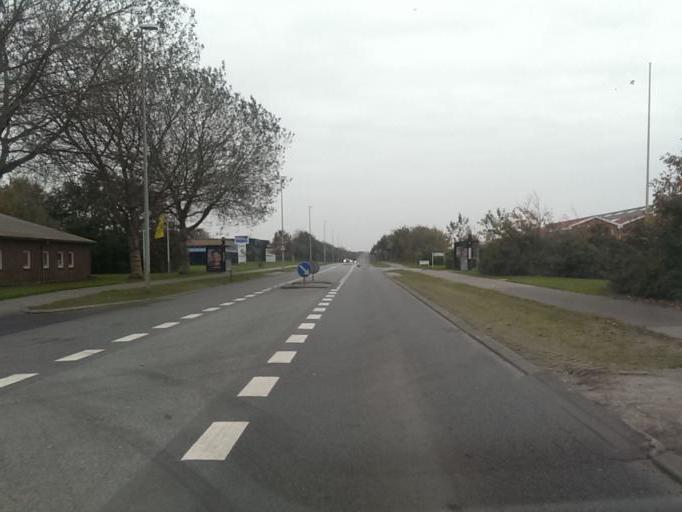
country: DK
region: South Denmark
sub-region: Esbjerg Kommune
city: Esbjerg
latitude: 55.5041
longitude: 8.4683
